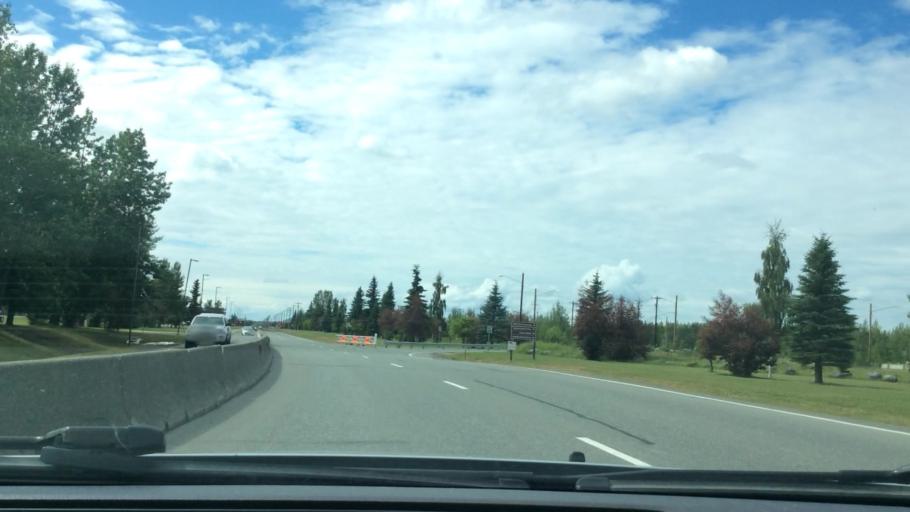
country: US
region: Alaska
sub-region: Anchorage Municipality
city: Elmendorf Air Force Base
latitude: 61.2588
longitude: -149.6676
